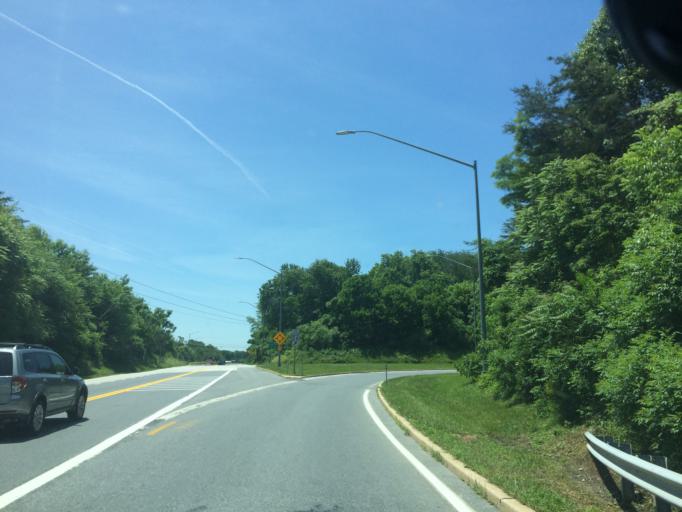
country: US
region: Maryland
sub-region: Carroll County
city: Eldersburg
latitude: 39.4313
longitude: -77.0064
